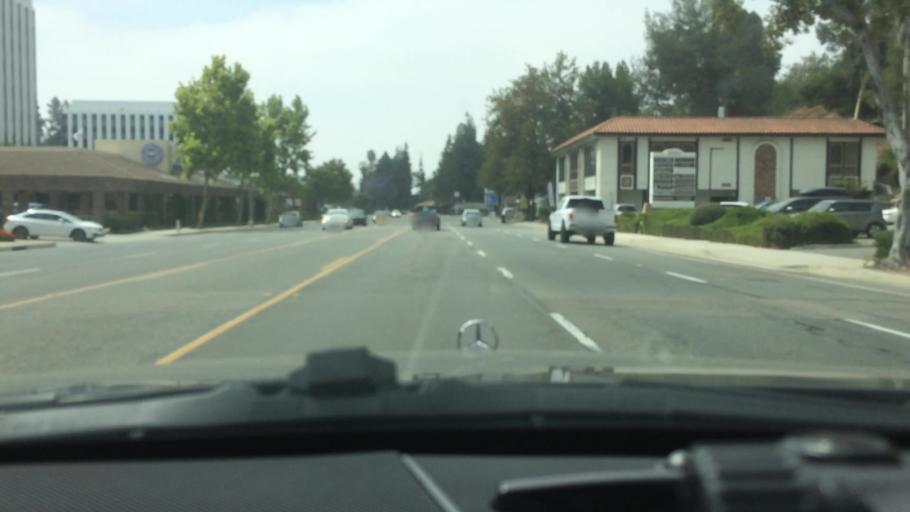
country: US
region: California
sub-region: Orange County
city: Fullerton
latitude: 33.8863
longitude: -117.9265
